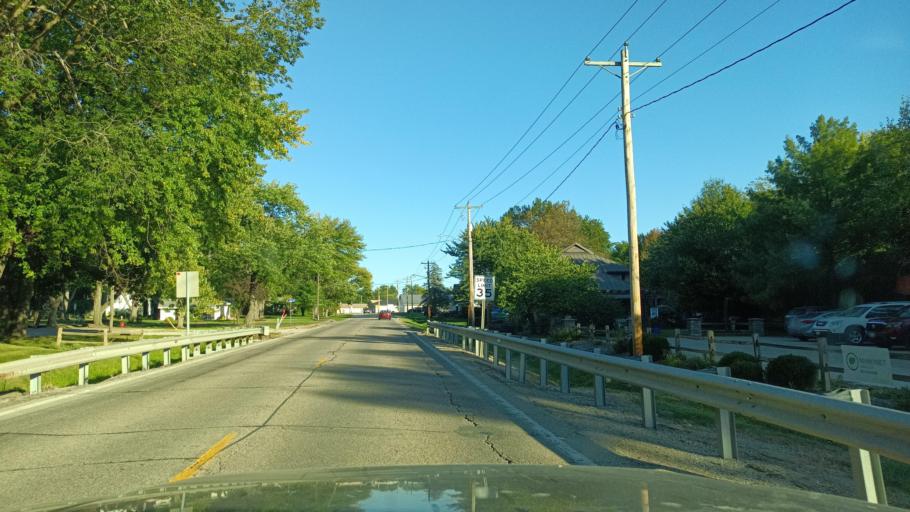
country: US
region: Illinois
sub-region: Champaign County
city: Mahomet
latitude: 40.1925
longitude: -88.4133
